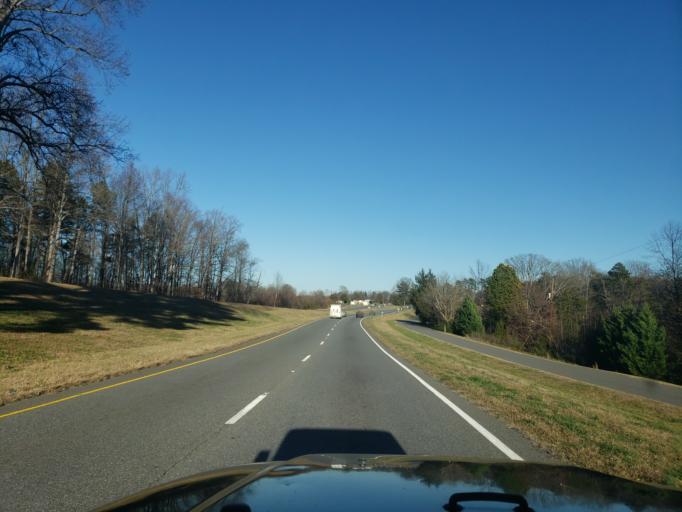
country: US
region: North Carolina
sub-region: Gaston County
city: Bessemer City
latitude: 35.2499
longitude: -81.2838
